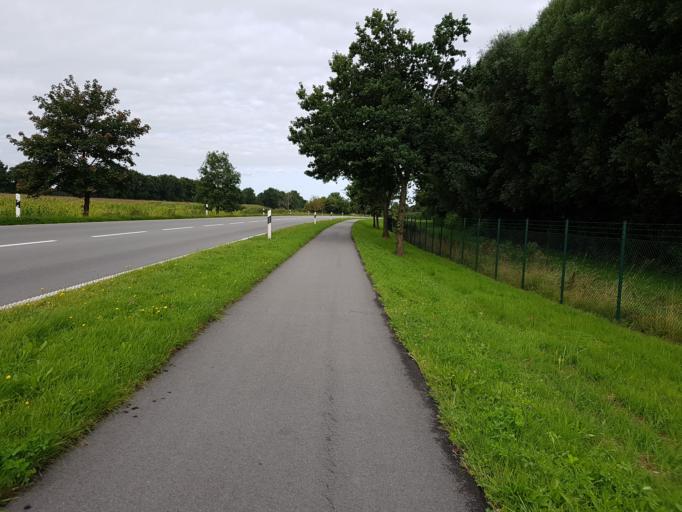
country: DE
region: Lower Saxony
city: Wittmund
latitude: 53.5683
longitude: 7.7752
